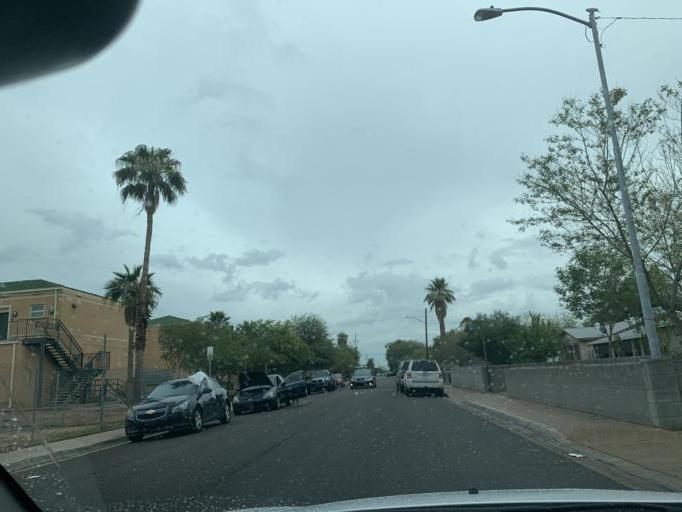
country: US
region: Arizona
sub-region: Maricopa County
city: Phoenix
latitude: 33.4605
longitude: -112.0495
